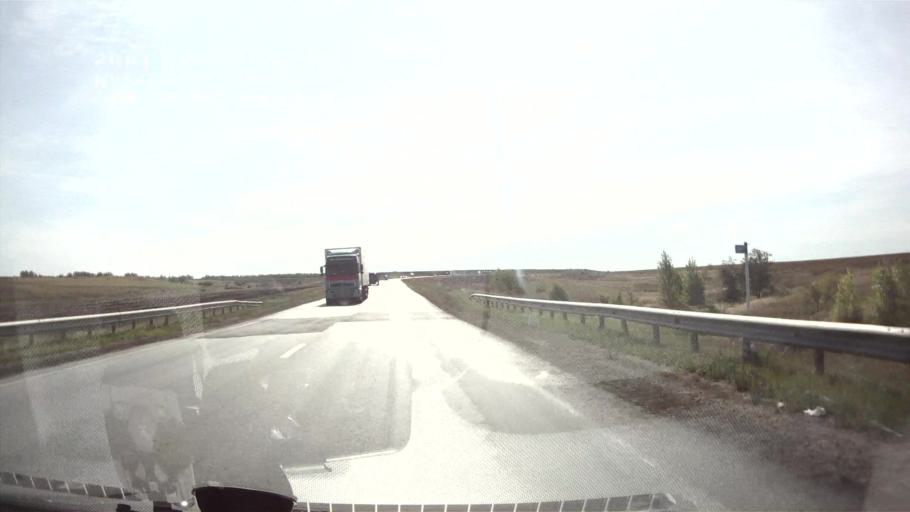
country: RU
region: Samara
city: Varlamovo
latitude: 53.0108
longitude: 48.3324
